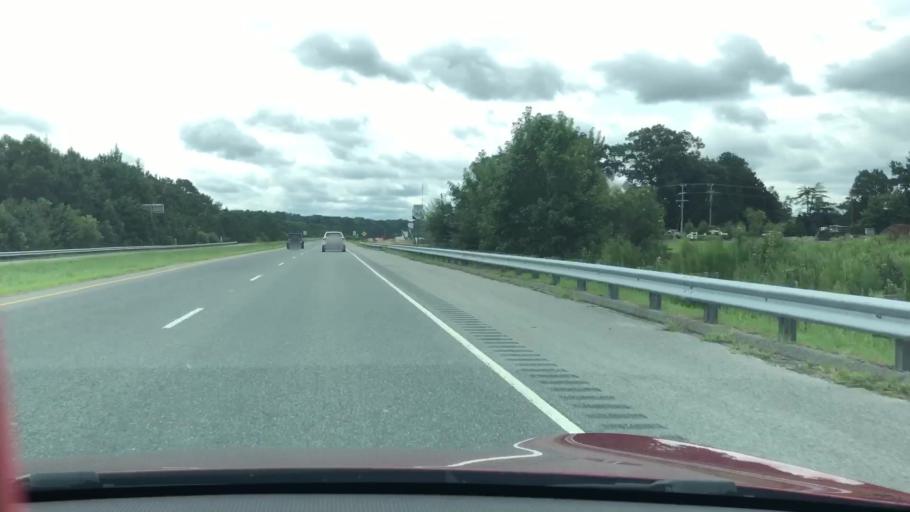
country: US
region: North Carolina
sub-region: Currituck County
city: Moyock
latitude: 36.6507
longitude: -76.2255
